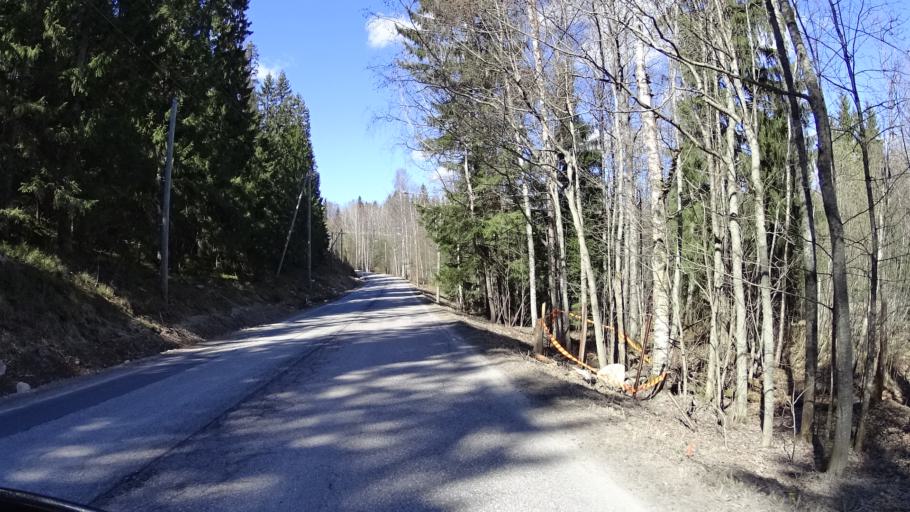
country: FI
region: Uusimaa
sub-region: Helsinki
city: Espoo
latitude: 60.2719
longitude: 24.5256
